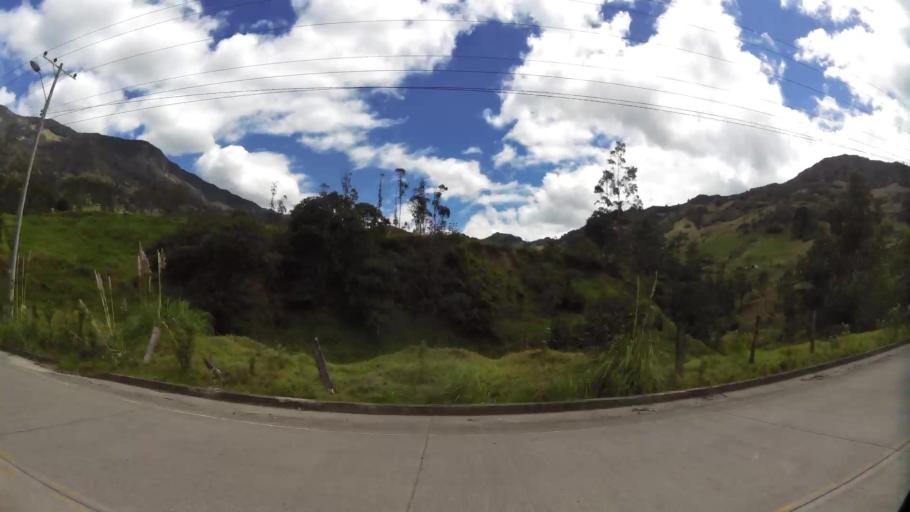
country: EC
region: Azuay
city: Cuenca
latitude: -3.1339
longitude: -79.1248
